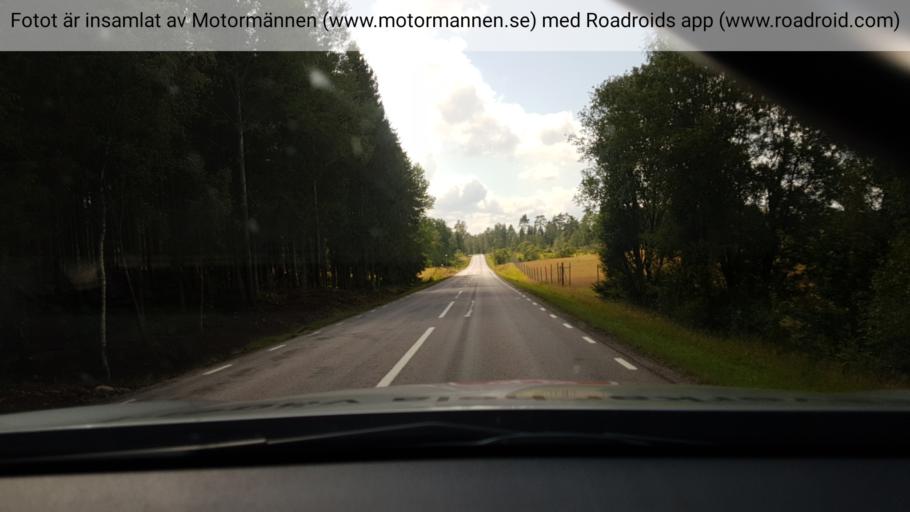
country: SE
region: Vaestra Goetaland
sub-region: Svenljunga Kommun
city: Svenljunga
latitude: 57.4949
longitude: 13.0762
